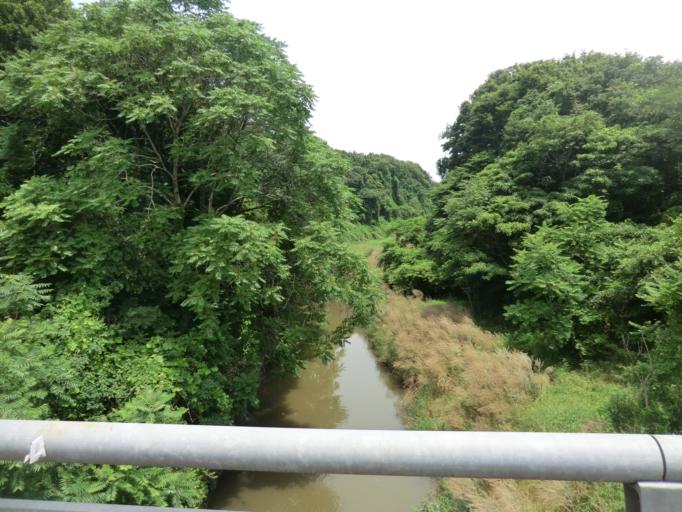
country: JP
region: Ibaraki
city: Iwai
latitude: 36.0577
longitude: 139.9122
